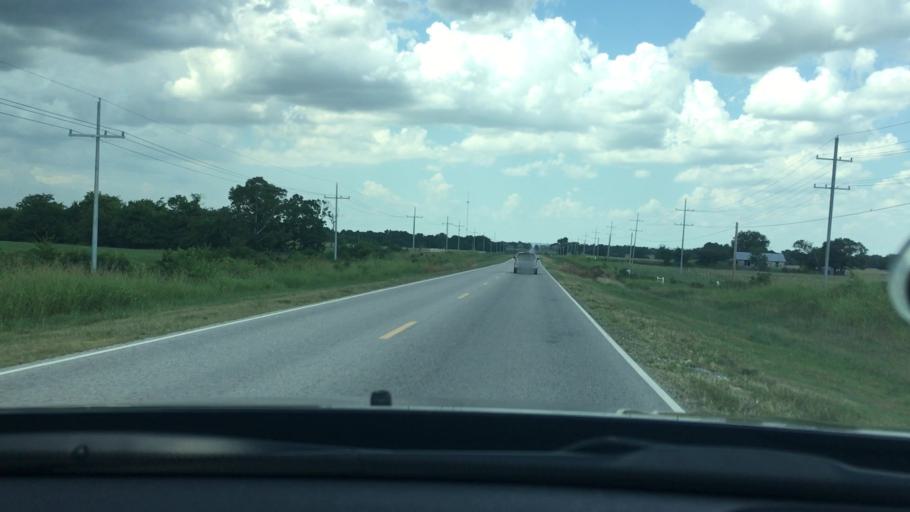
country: US
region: Oklahoma
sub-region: Pontotoc County
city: Ada
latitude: 34.6374
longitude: -96.6348
